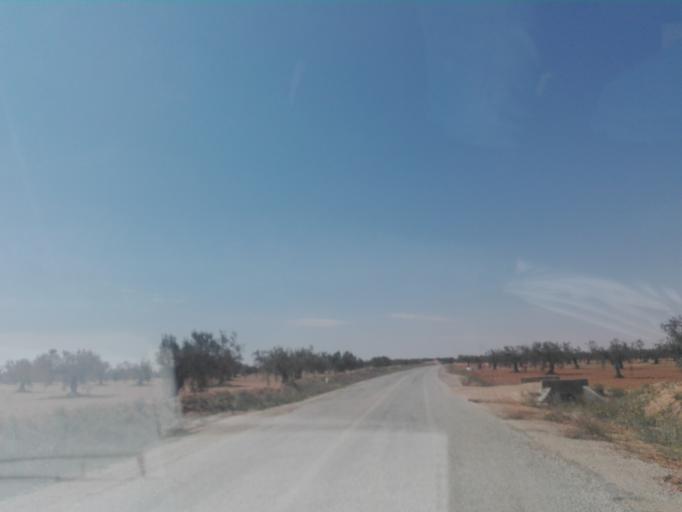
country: TN
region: Safaqis
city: Bi'r `Ali Bin Khalifah
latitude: 34.6498
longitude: 10.4134
